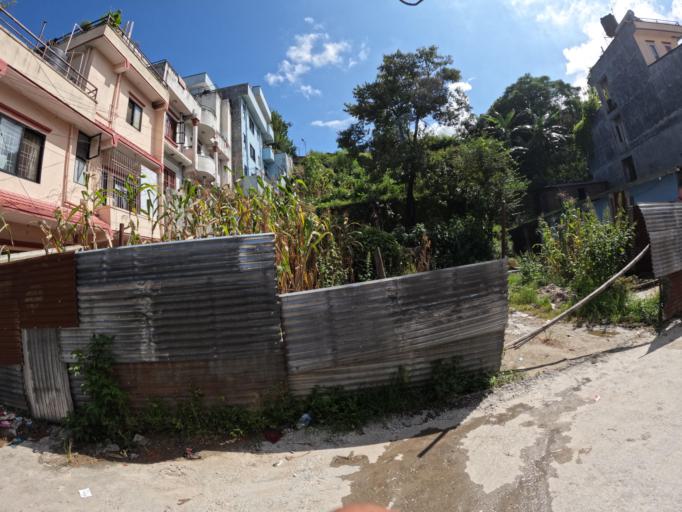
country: NP
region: Central Region
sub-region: Bagmati Zone
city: Kathmandu
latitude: 27.7479
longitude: 85.3329
